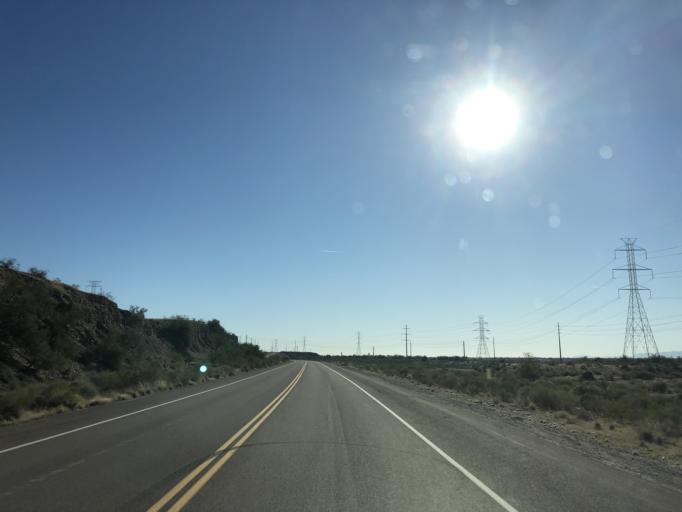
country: US
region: Arizona
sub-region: Maricopa County
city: Sun City West
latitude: 33.6883
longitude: -112.2960
